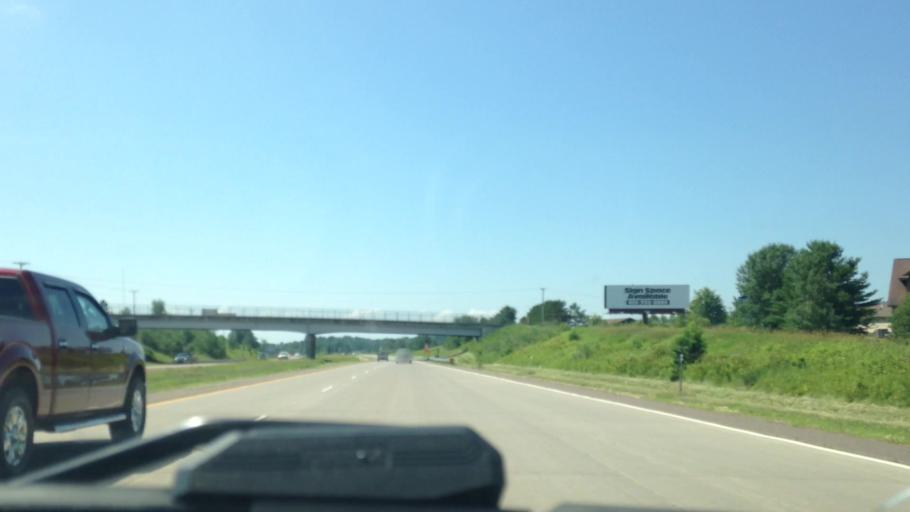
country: US
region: Wisconsin
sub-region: Barron County
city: Rice Lake
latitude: 45.5039
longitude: -91.7634
